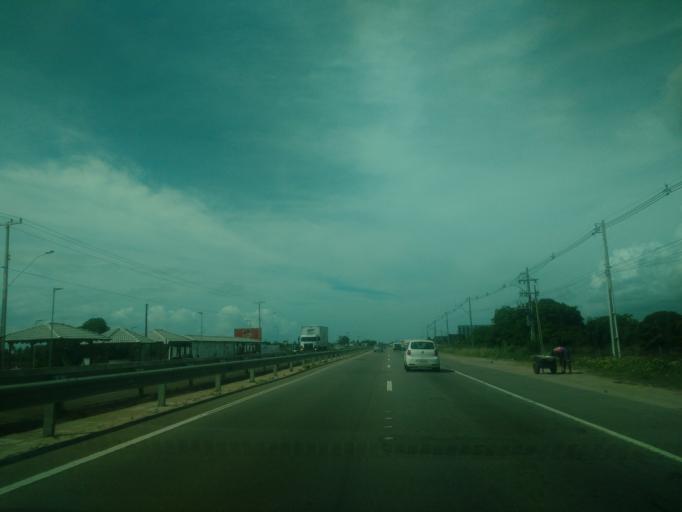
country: BR
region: Alagoas
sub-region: Marechal Deodoro
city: Marechal Deodoro
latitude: -9.7375
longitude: -35.8347
